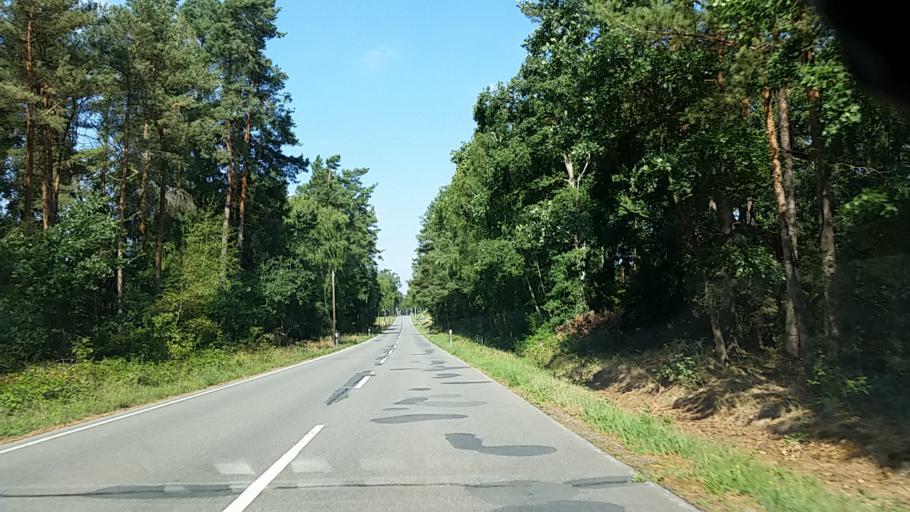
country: DE
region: Lower Saxony
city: Jelmstorf
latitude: 53.1229
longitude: 10.5371
